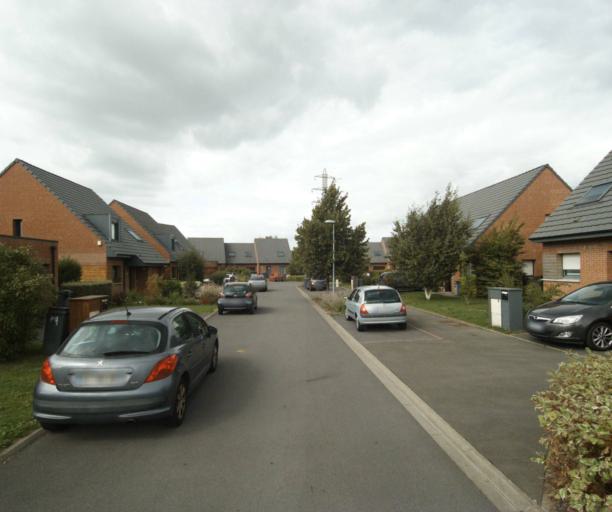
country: FR
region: Nord-Pas-de-Calais
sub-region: Departement du Nord
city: Saint-Andre-lez-Lille
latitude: 50.6712
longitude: 3.0415
